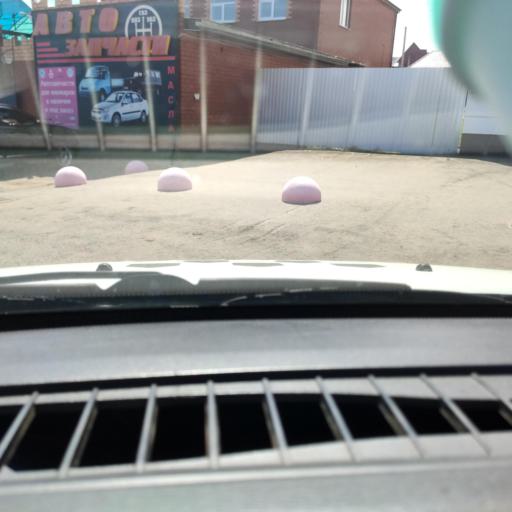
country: RU
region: Bashkortostan
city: Mesyagutovo
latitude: 55.5319
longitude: 58.2504
